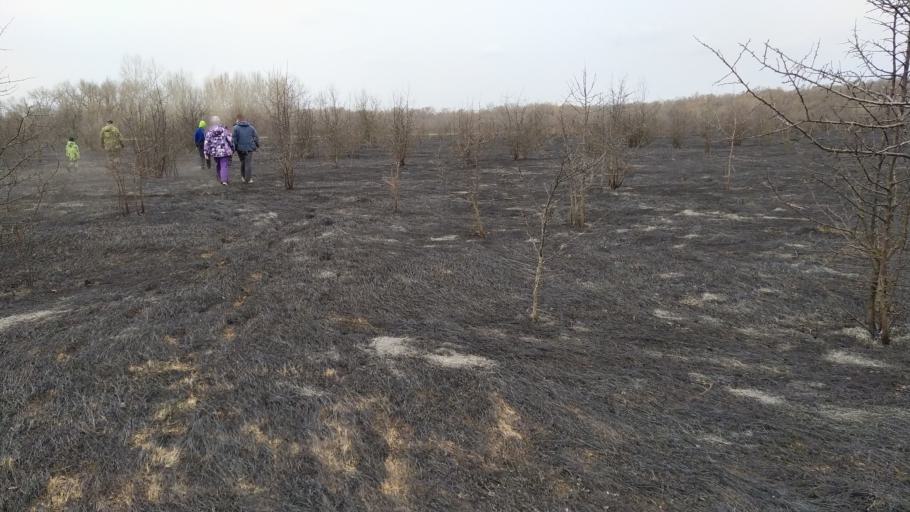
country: RU
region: Rostov
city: Semikarakorsk
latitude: 47.5416
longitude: 40.6835
